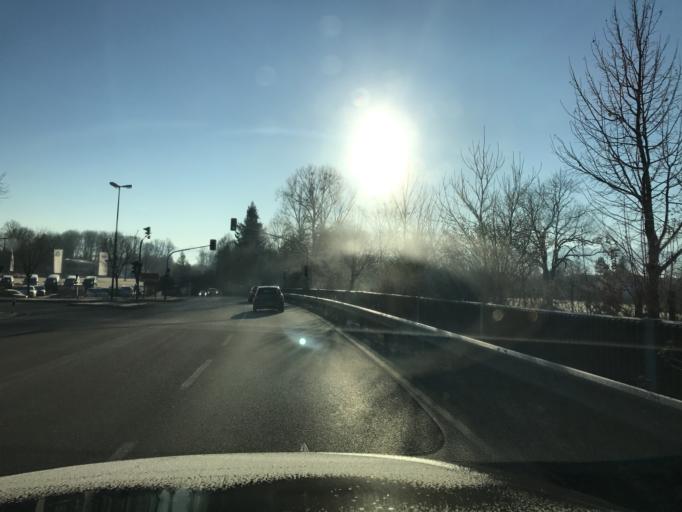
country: DE
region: Bavaria
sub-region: Upper Bavaria
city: Bad Aibling
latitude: 47.8586
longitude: 11.9883
